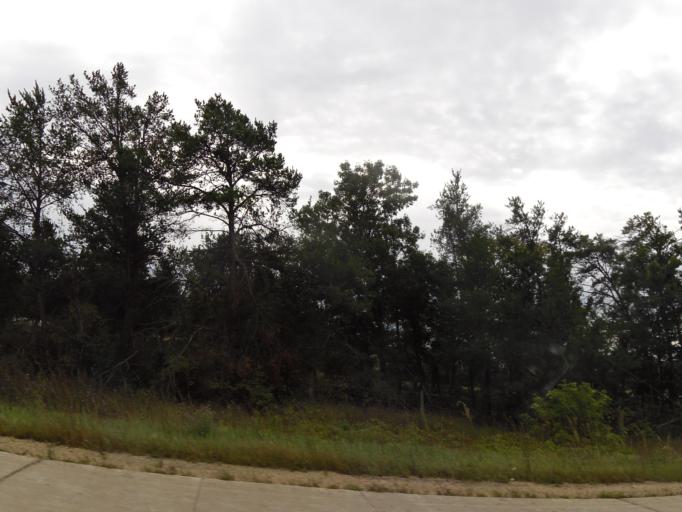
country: US
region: Wisconsin
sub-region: Monroe County
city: Sparta
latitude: 43.9361
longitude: -90.7724
